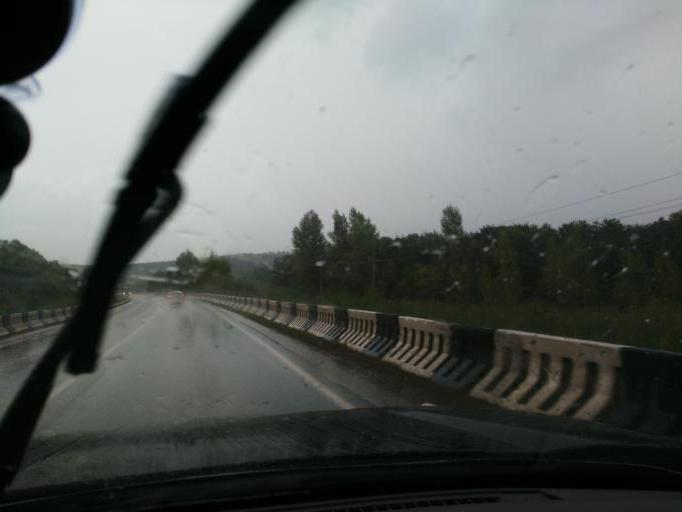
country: RU
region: Perm
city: Osa
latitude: 57.1803
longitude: 55.5739
